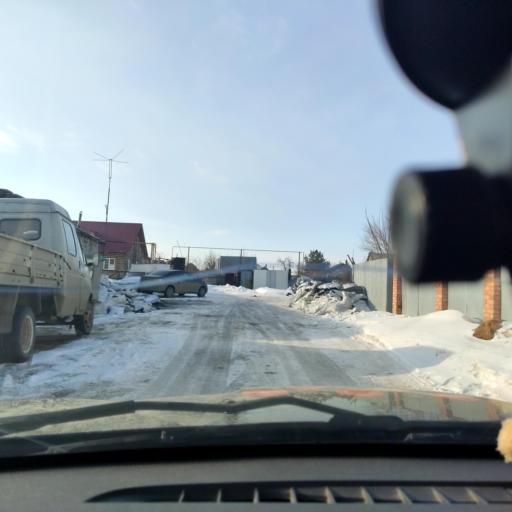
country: RU
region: Samara
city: Tol'yatti
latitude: 53.5742
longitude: 49.3209
